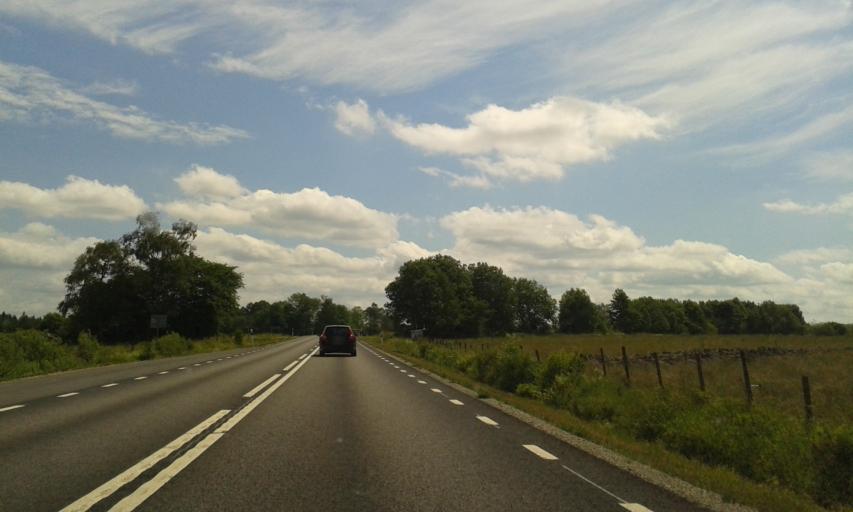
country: SE
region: Joenkoeping
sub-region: Varnamo Kommun
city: Rydaholm
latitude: 56.9977
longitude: 14.2843
